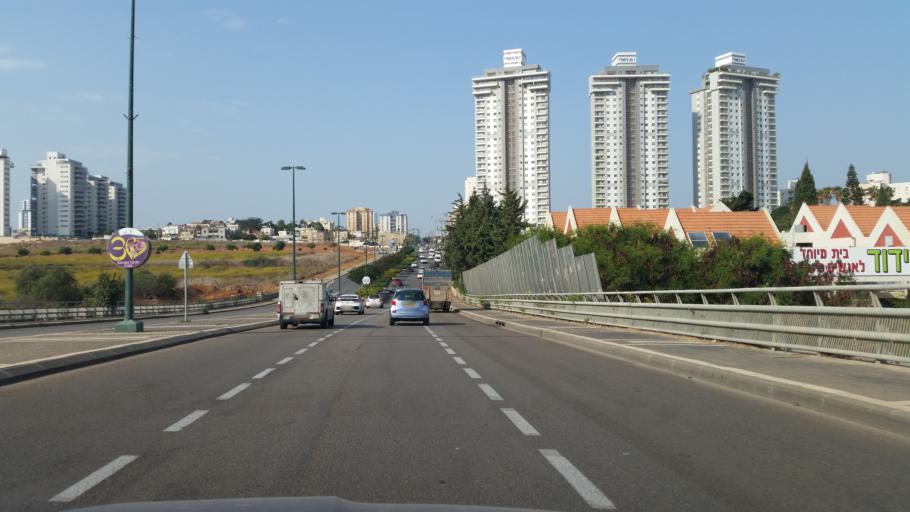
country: IL
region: Central District
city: Netanya
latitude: 32.3120
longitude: 34.8648
